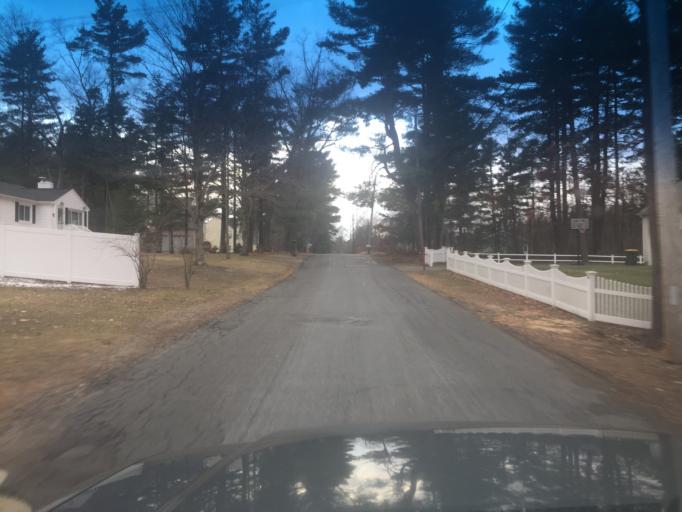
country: US
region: Massachusetts
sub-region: Norfolk County
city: Medway
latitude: 42.1234
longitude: -71.4376
